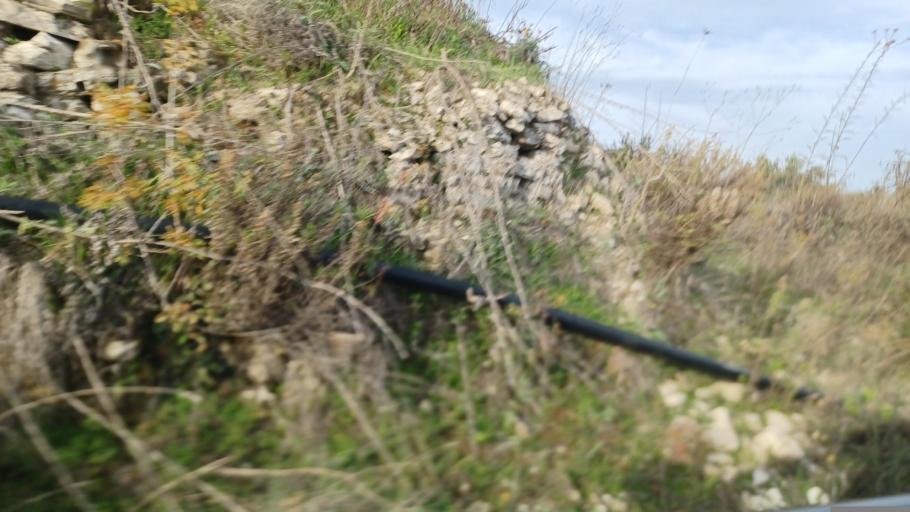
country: CY
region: Pafos
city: Mesogi
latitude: 34.8616
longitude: 32.5192
